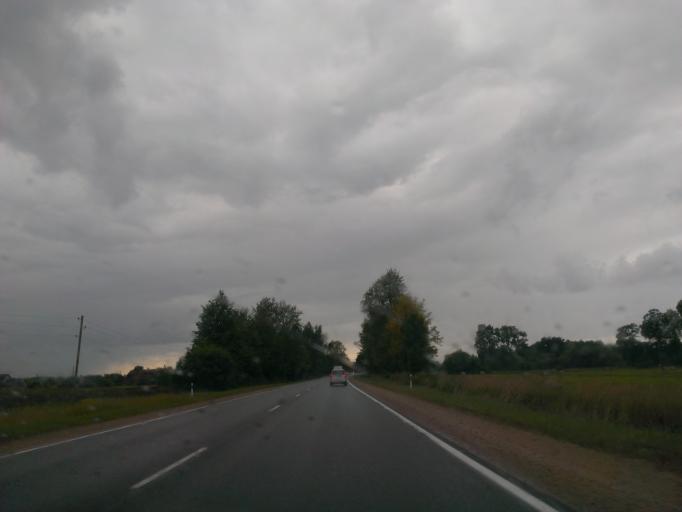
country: LV
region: Kegums
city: Kegums
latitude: 56.7715
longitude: 24.6682
